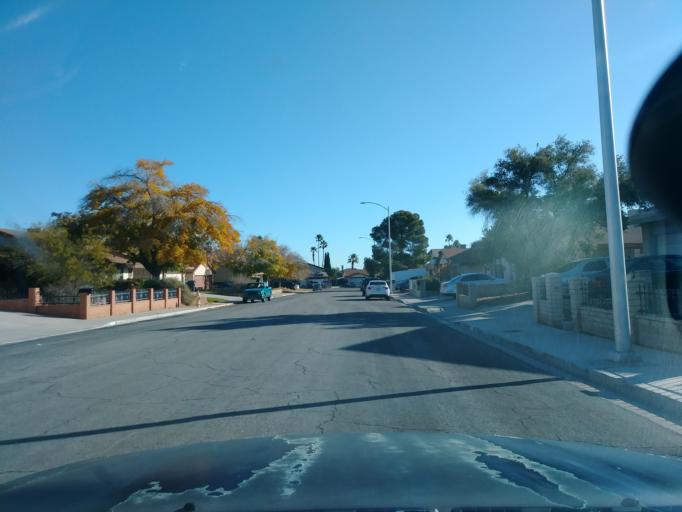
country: US
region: Nevada
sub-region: Clark County
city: Spring Valley
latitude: 36.1486
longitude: -115.2315
